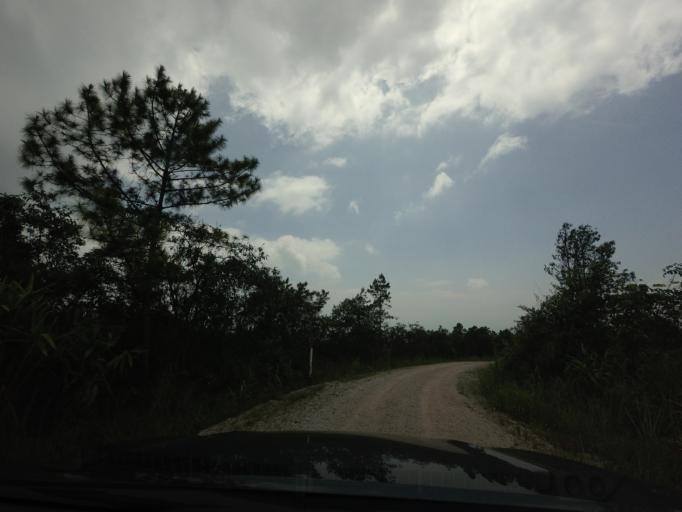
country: TH
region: Loei
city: Phu Ruea
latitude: 17.5041
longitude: 101.3423
